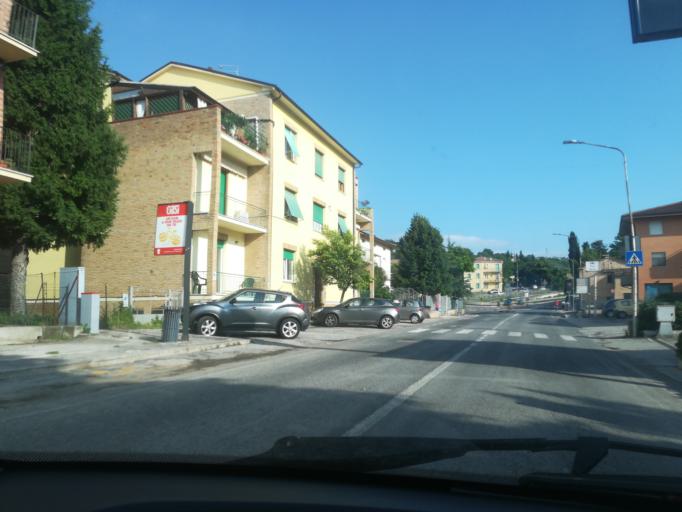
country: IT
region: The Marches
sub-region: Provincia di Macerata
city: Villa Potenza
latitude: 43.3212
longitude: 13.4269
